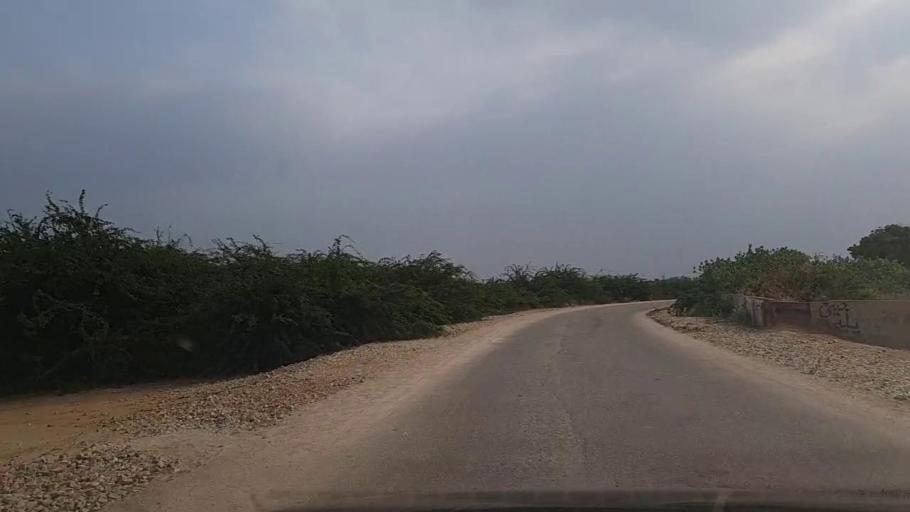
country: PK
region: Sindh
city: Thatta
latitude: 24.8539
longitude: 67.7783
